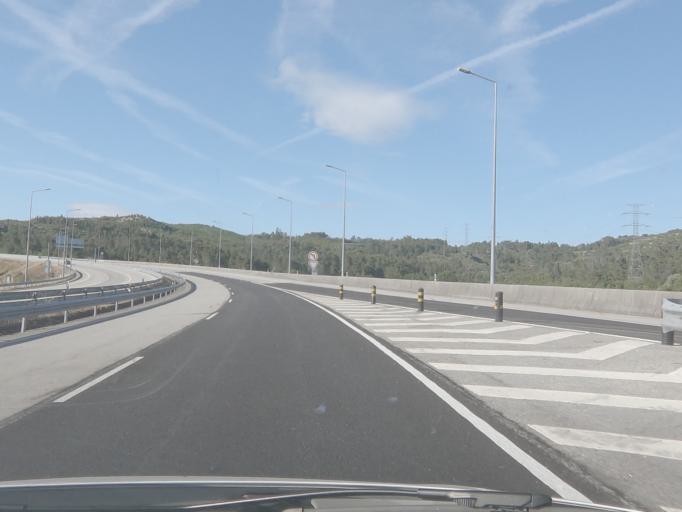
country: PT
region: Viseu
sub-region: Castro Daire
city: Castro Daire
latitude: 40.8230
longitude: -7.9361
